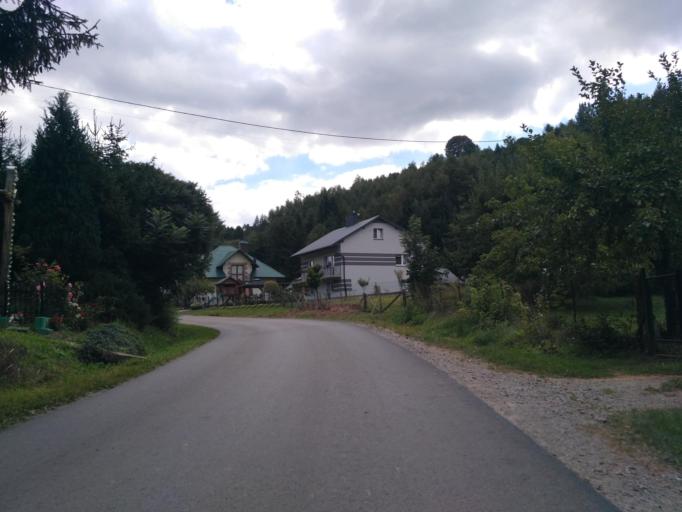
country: PL
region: Subcarpathian Voivodeship
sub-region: Powiat rzeszowski
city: Dynow
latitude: 49.7729
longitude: 22.2459
